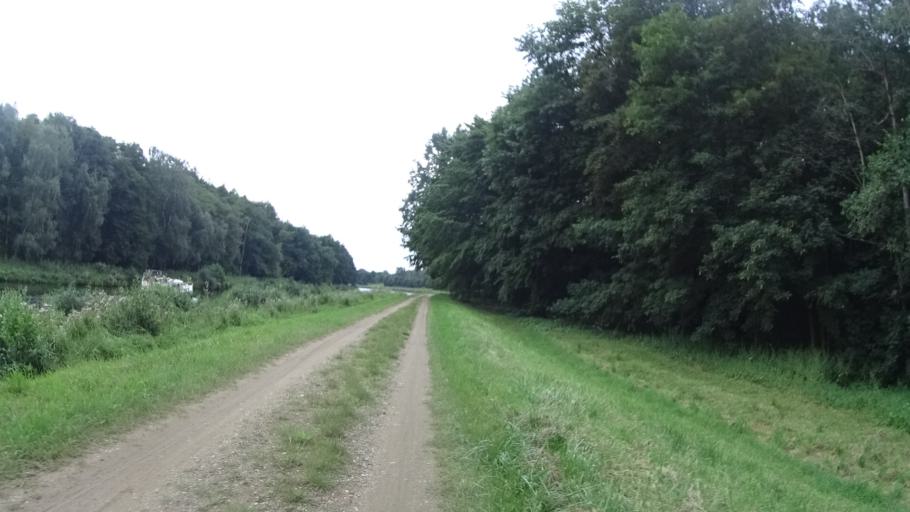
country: DE
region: Schleswig-Holstein
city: Lankau
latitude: 53.6497
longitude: 10.6470
